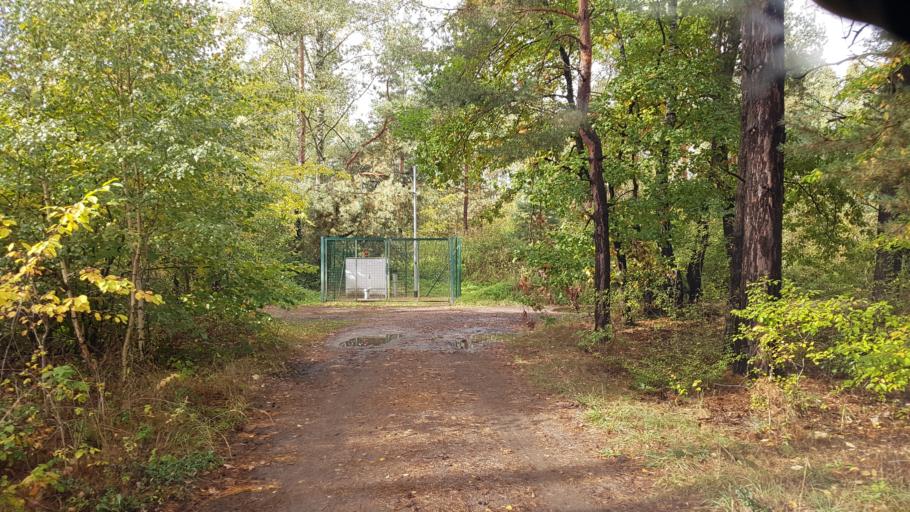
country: DE
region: Brandenburg
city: Grossraschen
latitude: 51.6043
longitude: 13.9979
